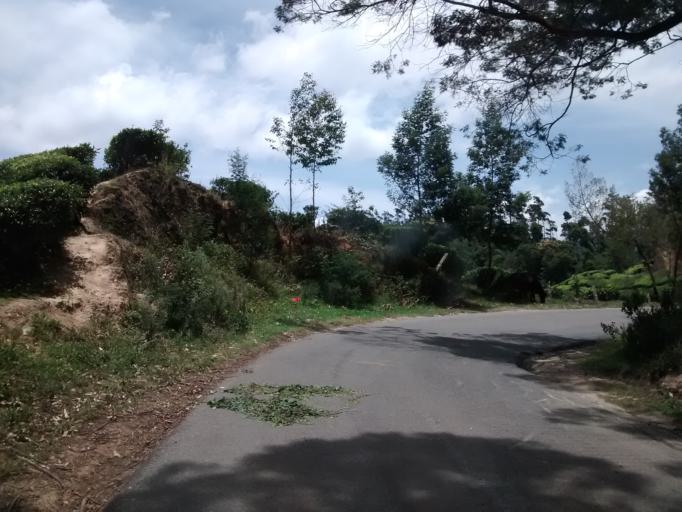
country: IN
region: Kerala
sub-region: Idukki
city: Munnar
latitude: 10.1301
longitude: 77.2271
